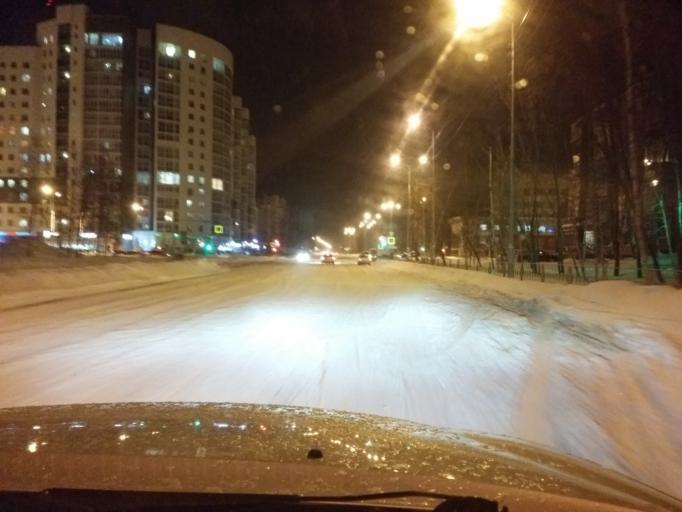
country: RU
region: Khanty-Mansiyskiy Avtonomnyy Okrug
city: Nizhnevartovsk
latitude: 60.9393
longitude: 76.5771
